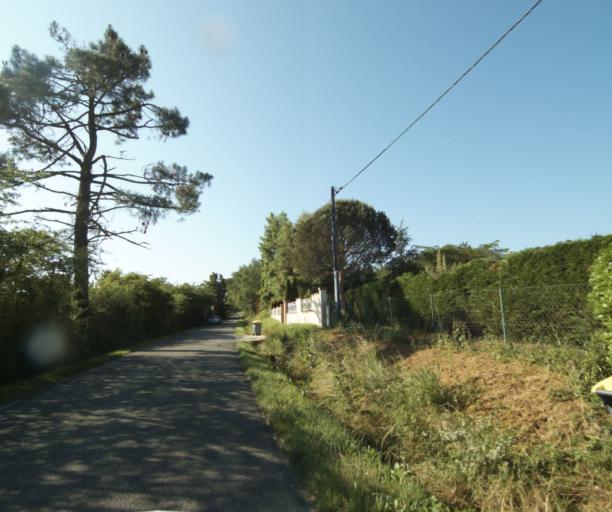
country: FR
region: Midi-Pyrenees
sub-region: Departement du Tarn-et-Garonne
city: Saint-Etienne-de-Tulmont
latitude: 44.0227
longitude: 1.4281
